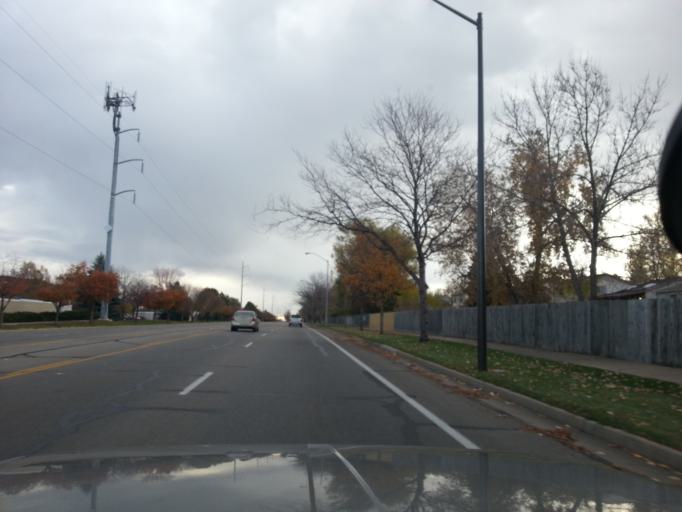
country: US
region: Colorado
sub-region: Larimer County
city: Fort Collins
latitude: 40.5527
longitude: -105.1022
